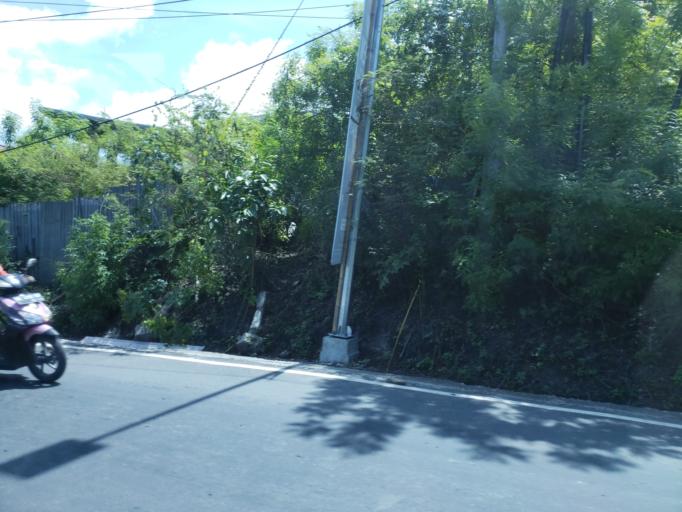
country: ID
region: Bali
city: Jimbaran
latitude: -8.7864
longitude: 115.1663
